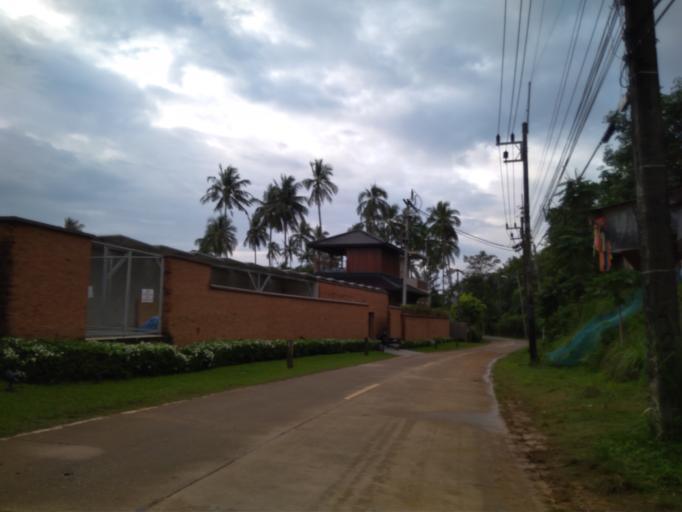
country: TH
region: Phangnga
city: Ko Yao
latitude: 8.1155
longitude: 98.6235
